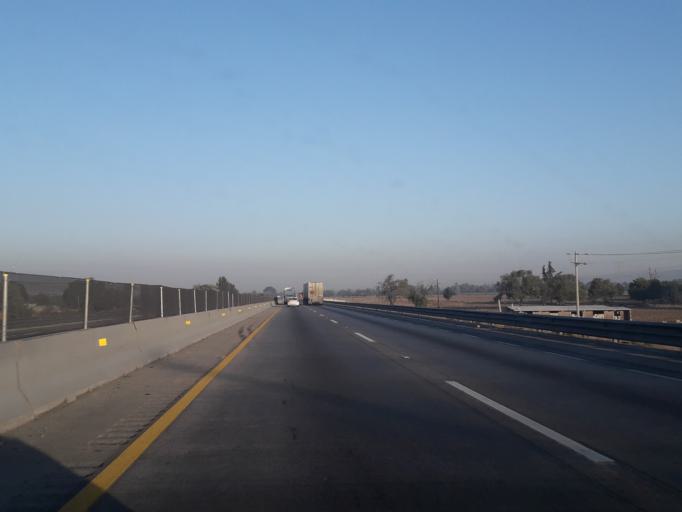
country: MX
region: Puebla
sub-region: Tepeaca
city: San Bartolome Hueyapan
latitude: 19.0164
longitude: -97.9313
